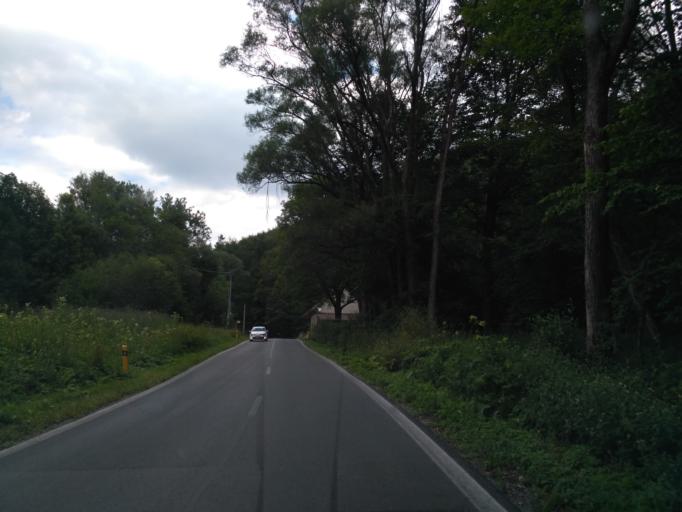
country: SK
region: Kosicky
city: Gelnica
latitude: 48.9086
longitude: 21.0292
